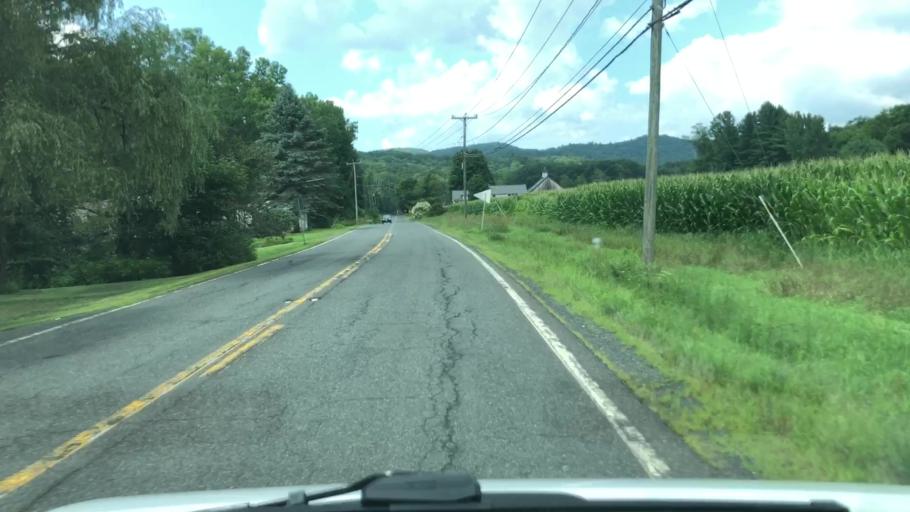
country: US
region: Massachusetts
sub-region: Franklin County
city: Conway
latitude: 42.5115
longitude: -72.7138
